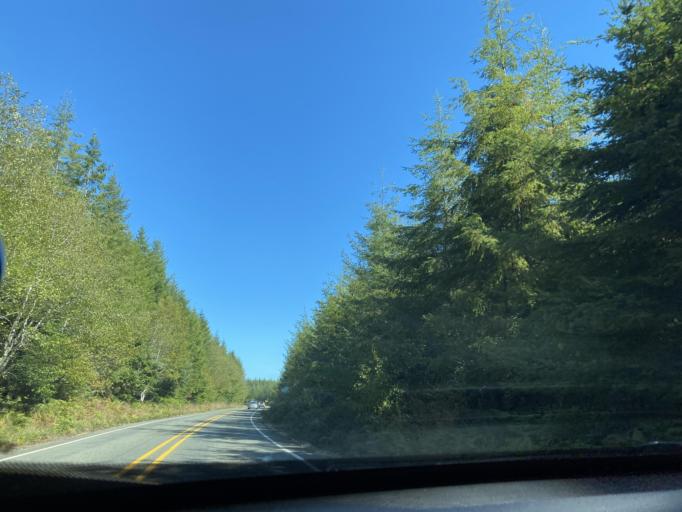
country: US
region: Washington
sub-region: Clallam County
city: Forks
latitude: 47.9388
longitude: -124.4665
